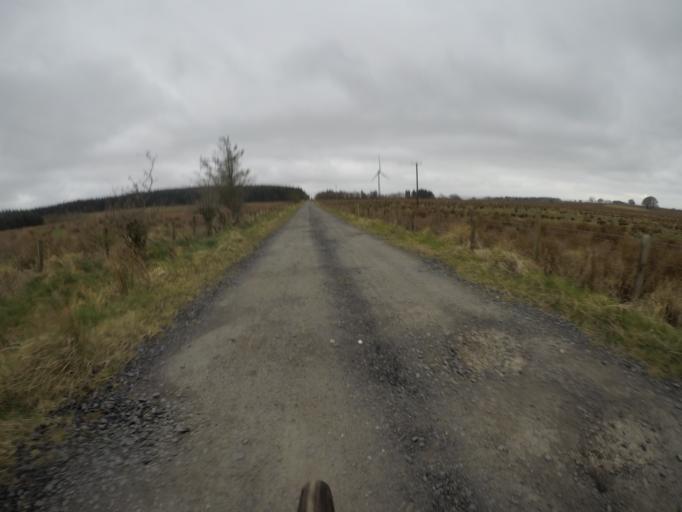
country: GB
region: Scotland
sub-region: East Ayrshire
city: Newmilns
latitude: 55.6308
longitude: -4.3418
